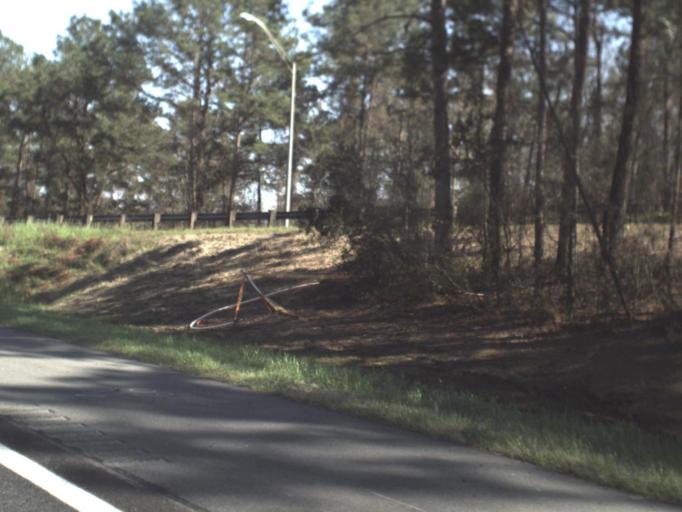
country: US
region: Florida
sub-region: Jackson County
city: Sneads
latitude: 30.6283
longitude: -84.8887
